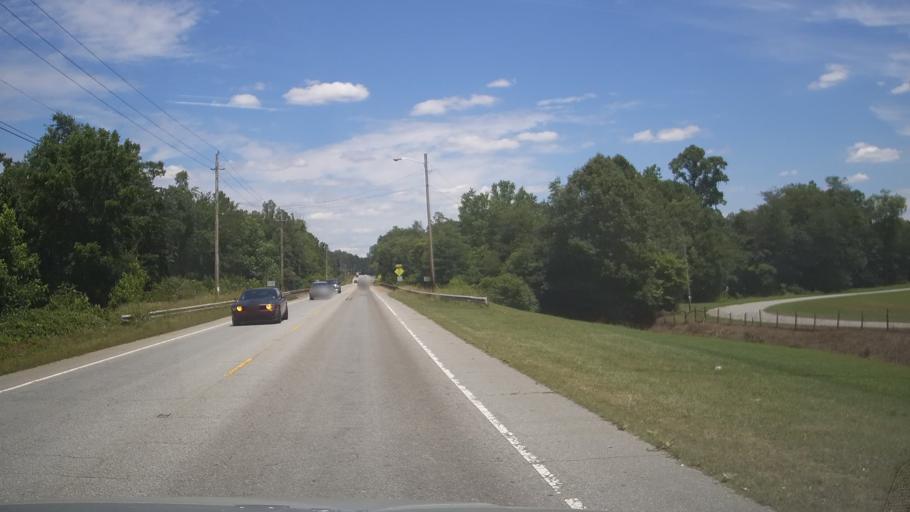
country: US
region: North Carolina
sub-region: Burke County
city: Morganton
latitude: 35.7387
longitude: -81.7250
